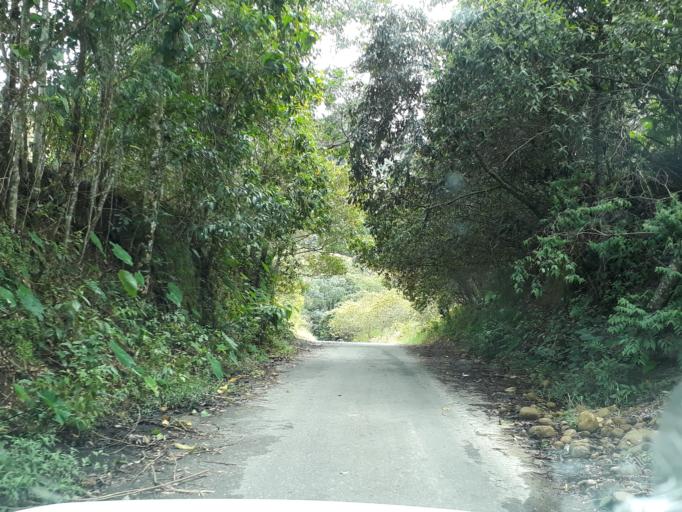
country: CO
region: Cundinamarca
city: Medina
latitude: 4.5781
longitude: -73.3444
